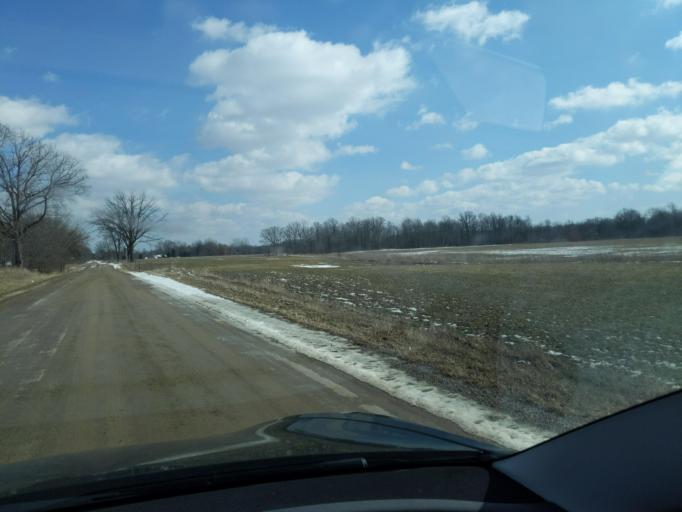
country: US
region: Michigan
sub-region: Ingham County
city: Webberville
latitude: 42.6138
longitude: -84.1443
